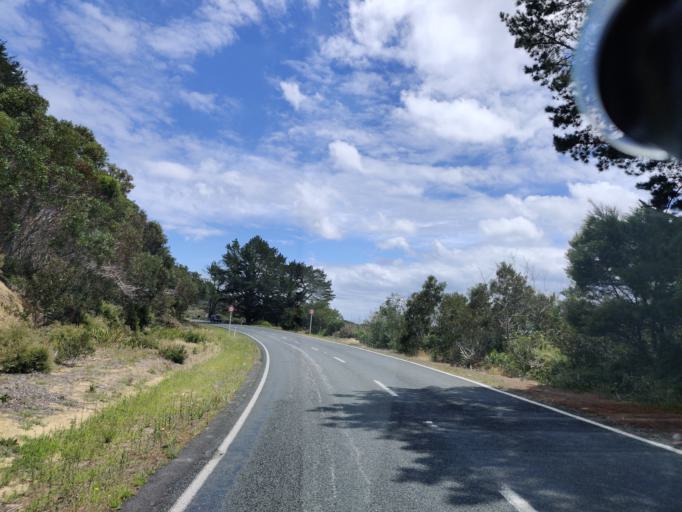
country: NZ
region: Northland
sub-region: Far North District
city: Kaitaia
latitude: -34.8050
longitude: 173.1145
